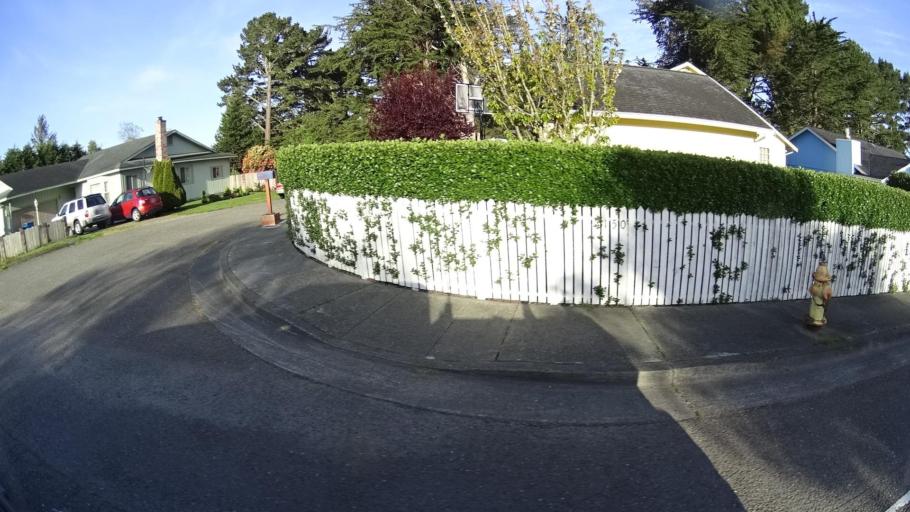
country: US
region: California
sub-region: Humboldt County
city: Humboldt Hill
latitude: 40.7188
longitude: -124.2033
